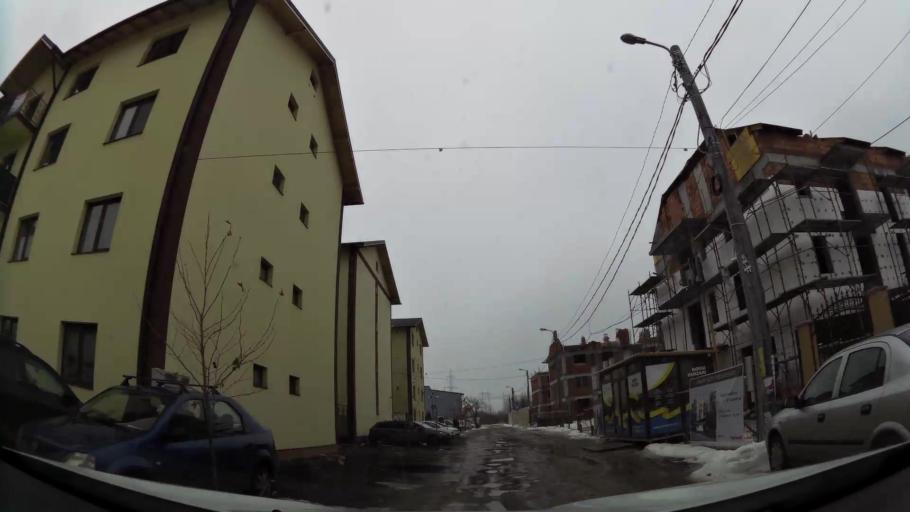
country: RO
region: Ilfov
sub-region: Comuna Popesti-Leordeni
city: Popesti-Leordeni
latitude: 44.4032
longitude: 26.1683
